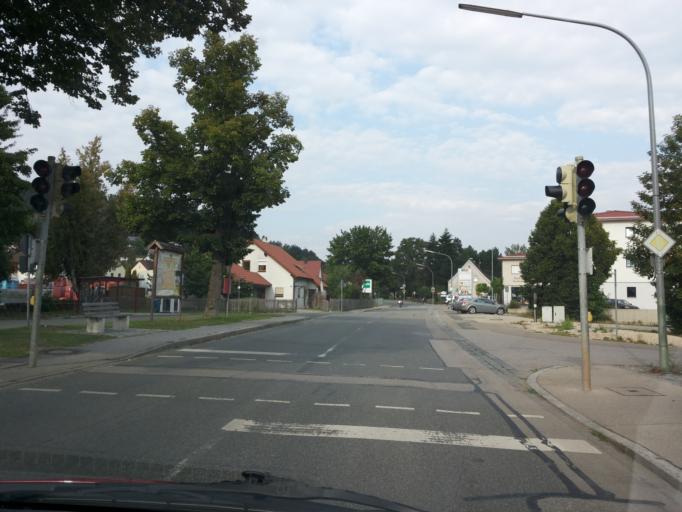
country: DE
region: Bavaria
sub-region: Upper Palatinate
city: Dietfurt
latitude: 49.0343
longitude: 11.5799
